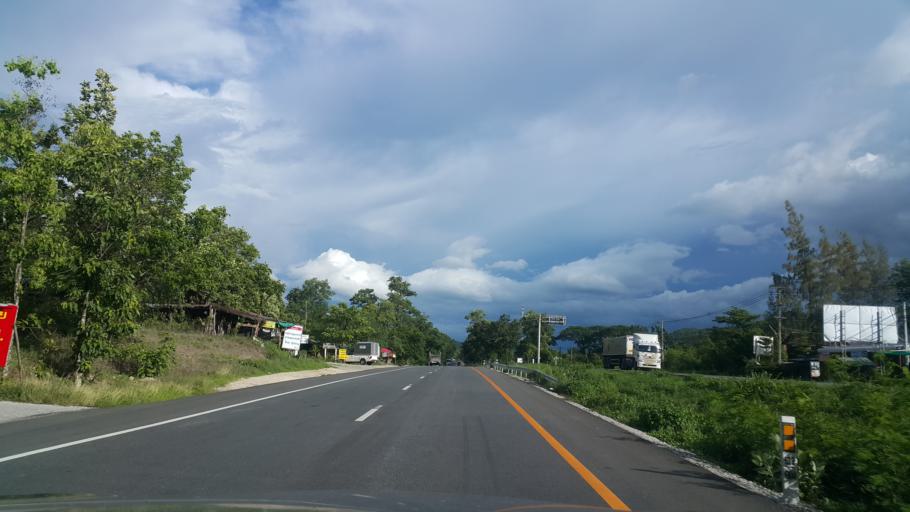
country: TH
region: Tak
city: Ban Tak
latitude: 17.0062
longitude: 99.1095
